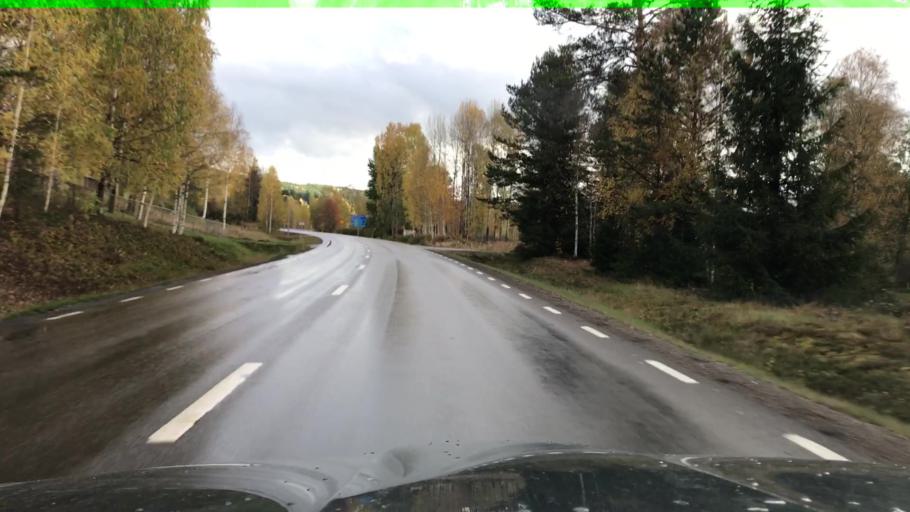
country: SE
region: Vaermland
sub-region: Hagfors Kommun
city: Ekshaerad
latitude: 60.4251
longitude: 13.2526
